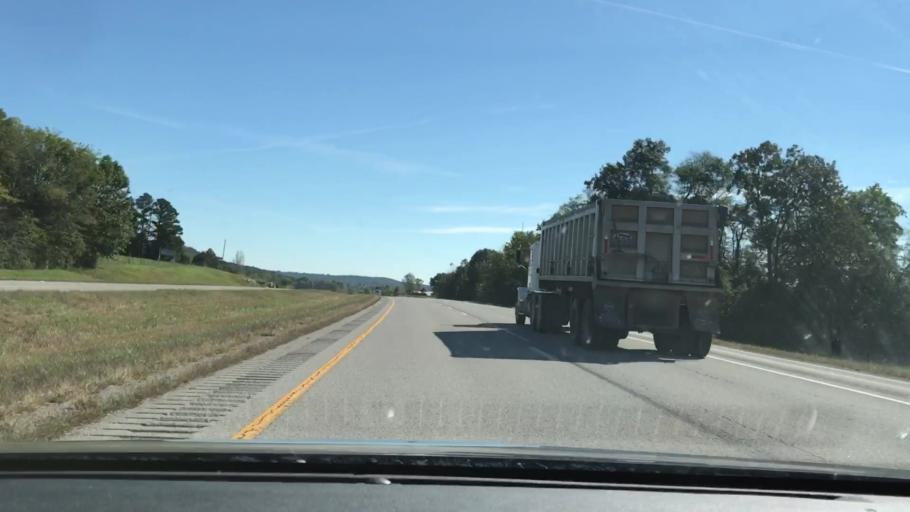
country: US
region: Kentucky
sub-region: Todd County
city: Elkton
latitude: 36.8459
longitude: -87.2918
